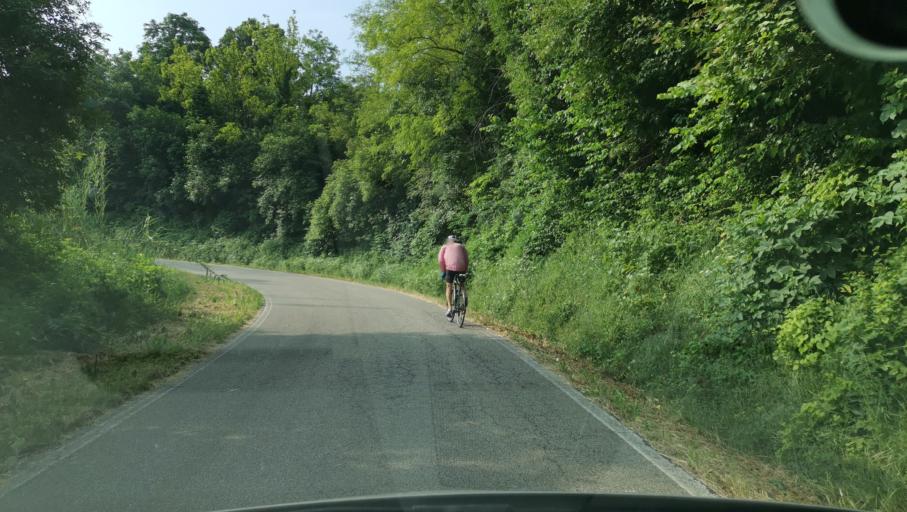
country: IT
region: Piedmont
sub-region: Provincia di Asti
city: Moncalvo
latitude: 45.0546
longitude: 8.2518
